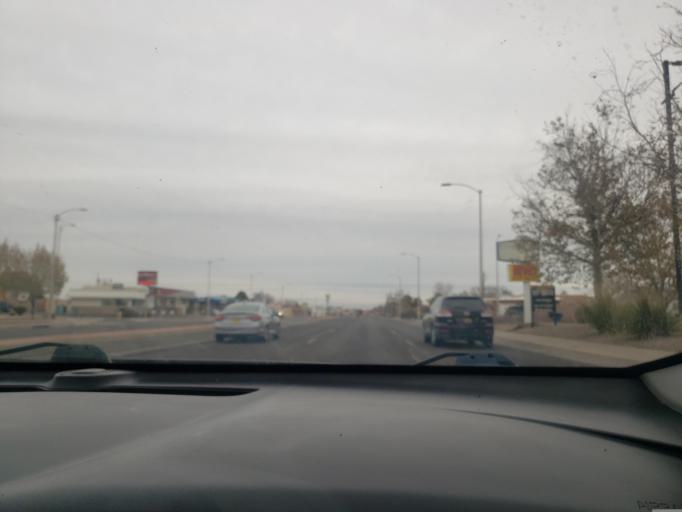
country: US
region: New Mexico
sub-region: Bernalillo County
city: Albuquerque
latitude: 35.0887
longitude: -106.5861
